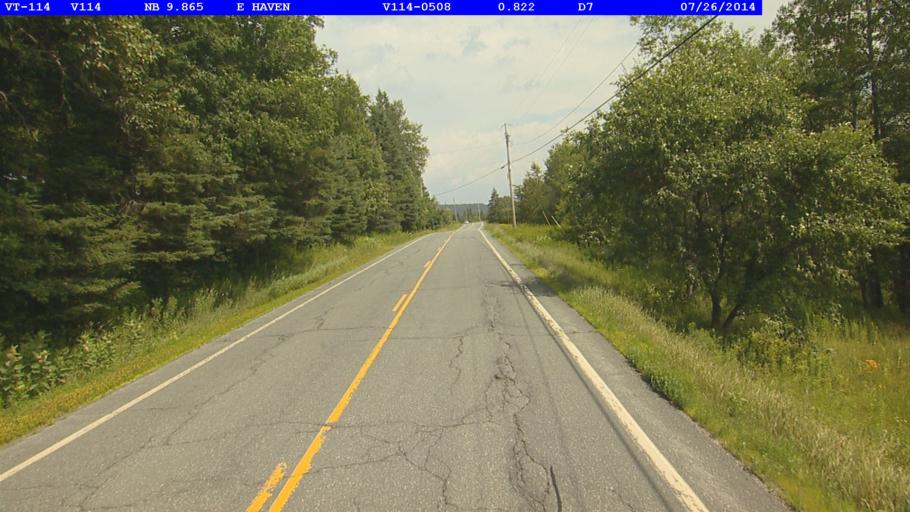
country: US
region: Vermont
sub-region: Caledonia County
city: Lyndonville
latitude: 44.6507
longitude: -71.8923
